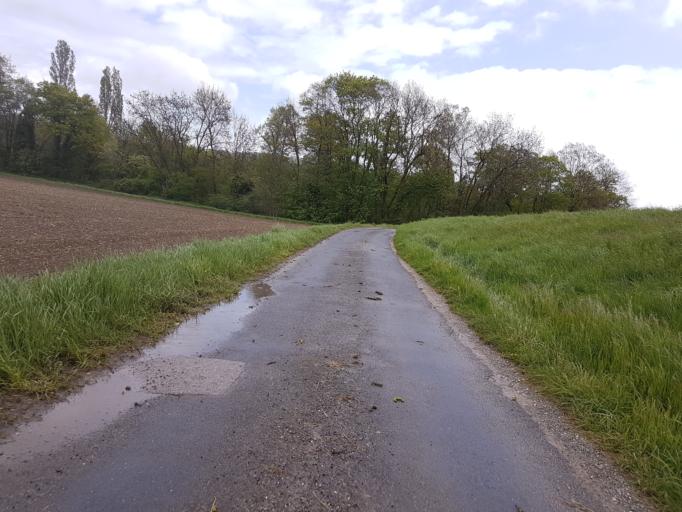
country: CH
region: Vaud
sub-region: Morges District
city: La Sarraz
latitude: 46.6495
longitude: 6.5158
